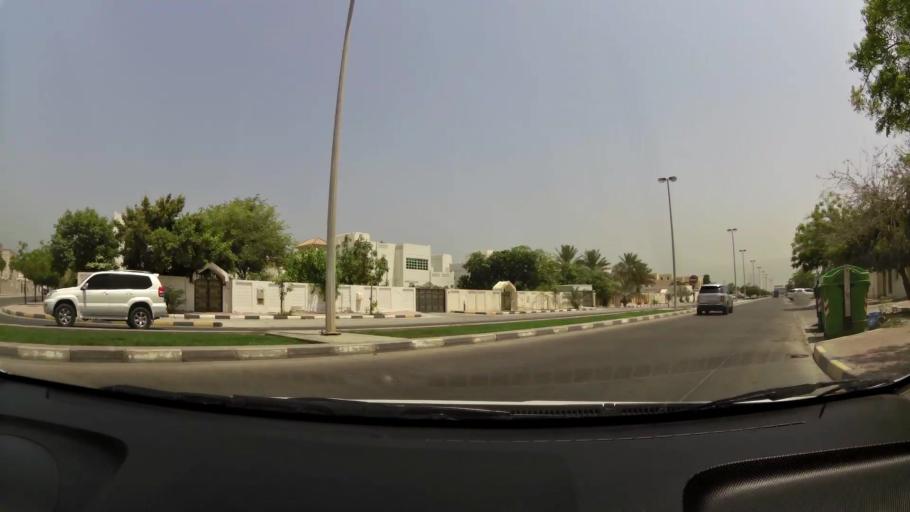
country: AE
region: Ash Shariqah
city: Sharjah
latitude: 25.3435
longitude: 55.3701
